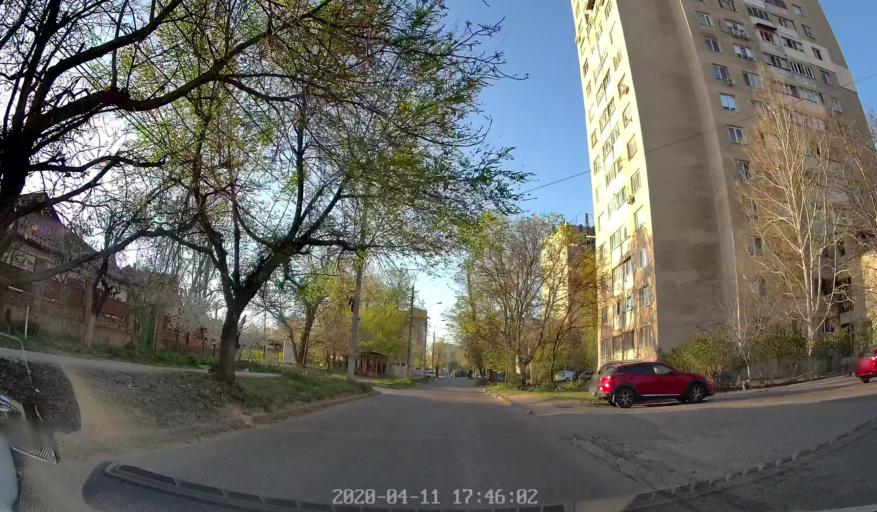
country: MD
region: Chisinau
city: Chisinau
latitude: 46.9895
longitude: 28.8212
